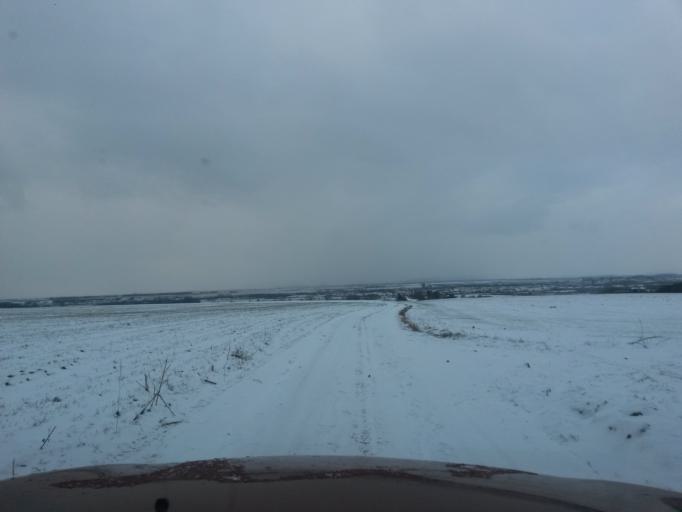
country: SK
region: Kosicky
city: Kosice
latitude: 48.6007
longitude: 21.3653
